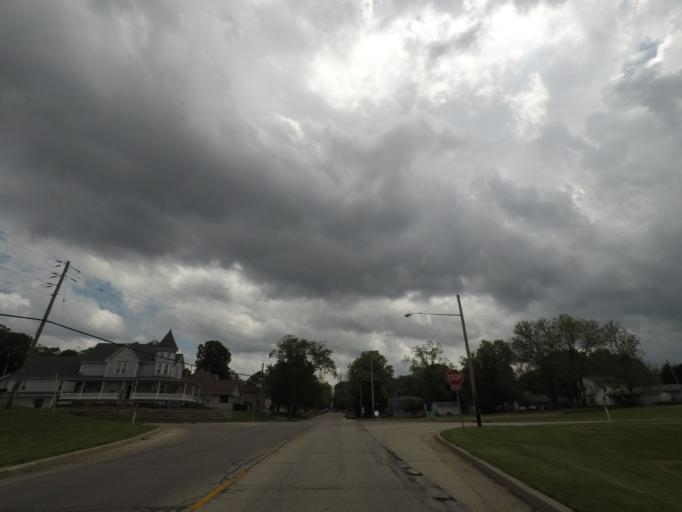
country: US
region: Illinois
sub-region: De Witt County
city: Clinton
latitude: 40.1603
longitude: -88.9606
